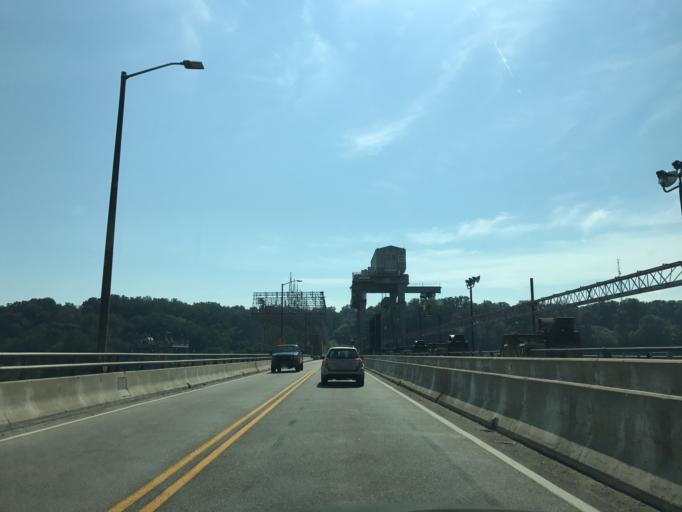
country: US
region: Maryland
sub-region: Cecil County
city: Rising Sun
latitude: 39.6603
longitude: -76.1738
